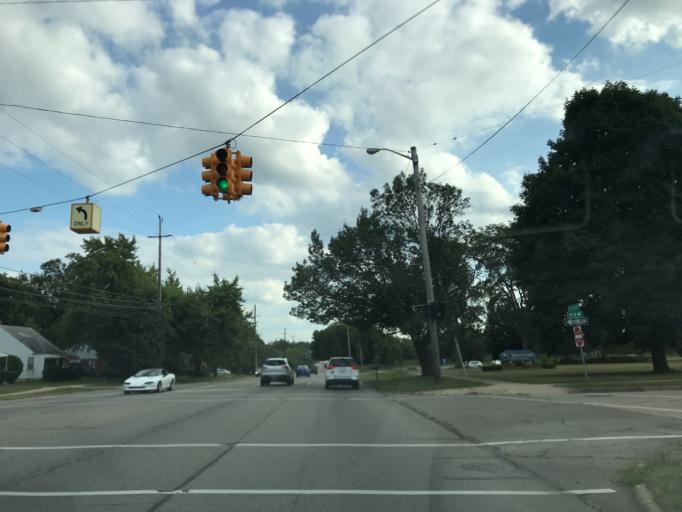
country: US
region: Michigan
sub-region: Wayne County
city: Redford
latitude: 42.3964
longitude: -83.2959
